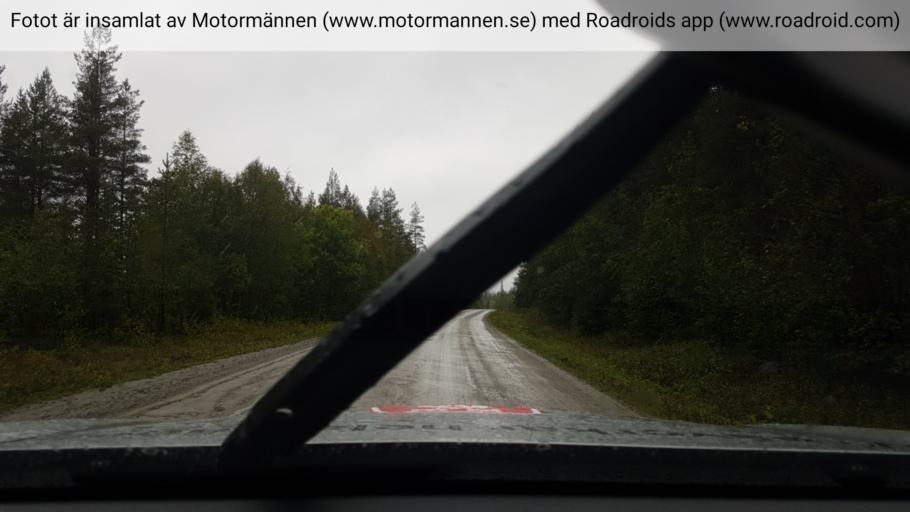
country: SE
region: Vaesternorrland
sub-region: OErnskoeldsviks Kommun
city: Bredbyn
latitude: 64.0690
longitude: 18.1245
